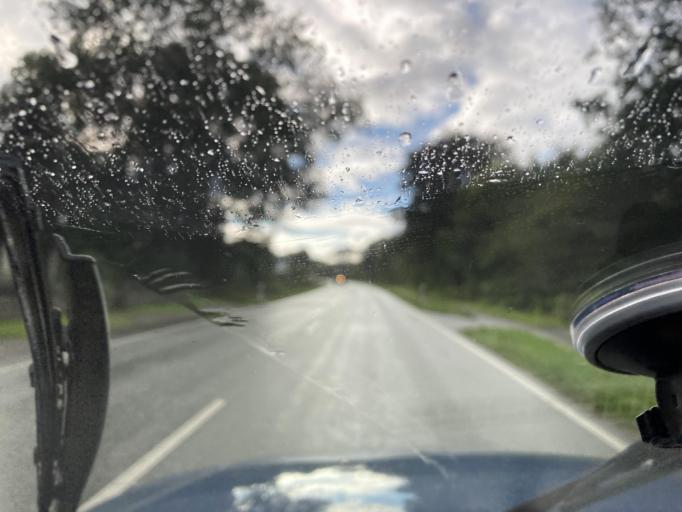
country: DE
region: Schleswig-Holstein
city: Tellingstedt
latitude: 54.2197
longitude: 9.3076
